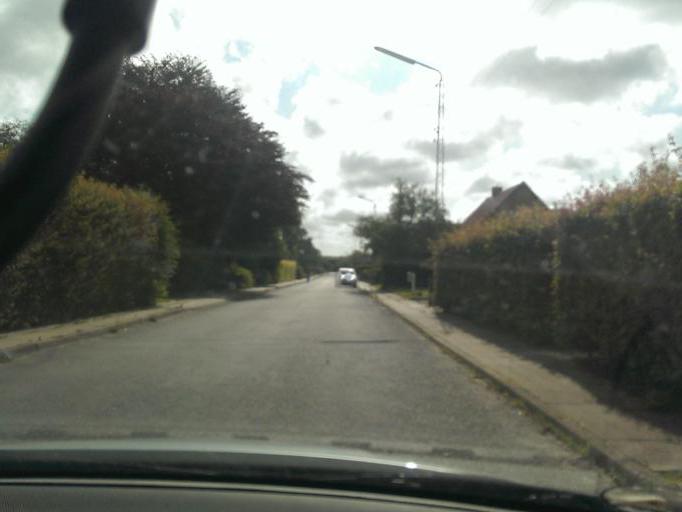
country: DK
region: North Denmark
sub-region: Hjorring Kommune
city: Vra
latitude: 57.3510
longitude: 9.9426
